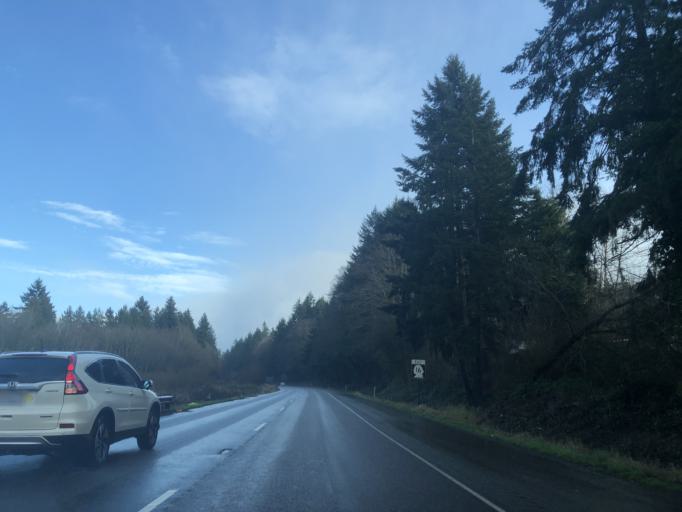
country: US
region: Washington
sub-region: Kitsap County
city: Navy Yard City
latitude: 47.5275
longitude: -122.6791
